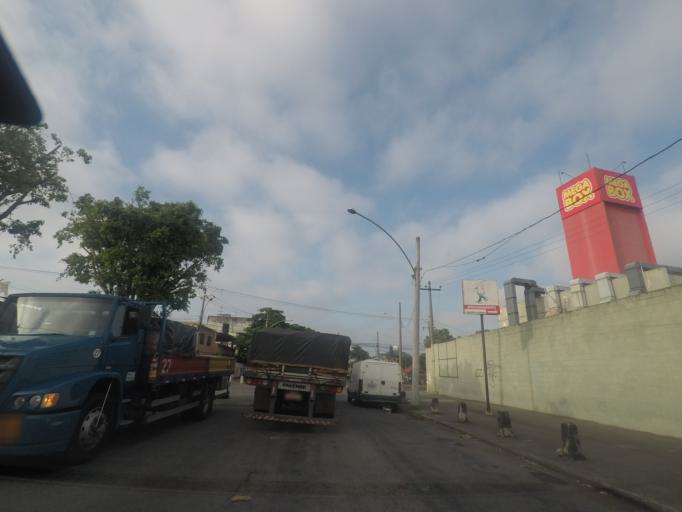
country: BR
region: Rio de Janeiro
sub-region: Duque De Caxias
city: Duque de Caxias
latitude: -22.8364
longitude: -43.2633
